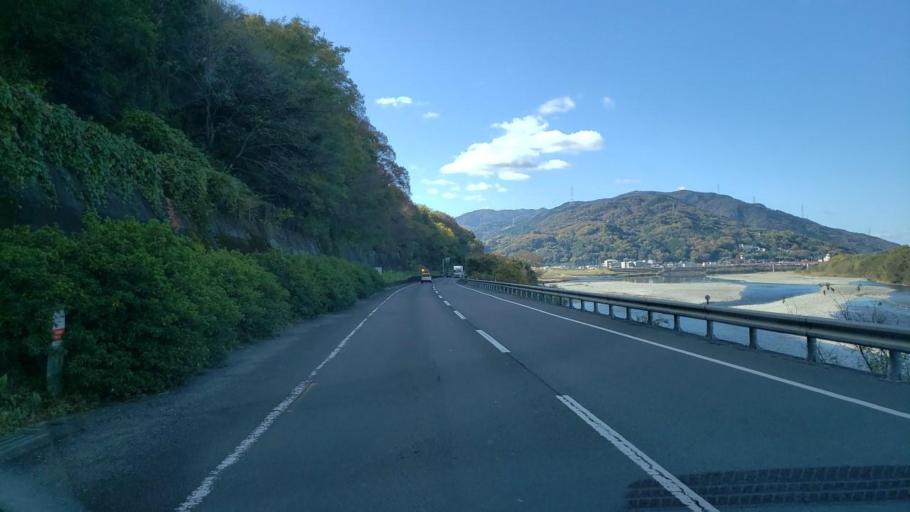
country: JP
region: Tokushima
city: Wakimachi
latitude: 34.0606
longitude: 134.1865
